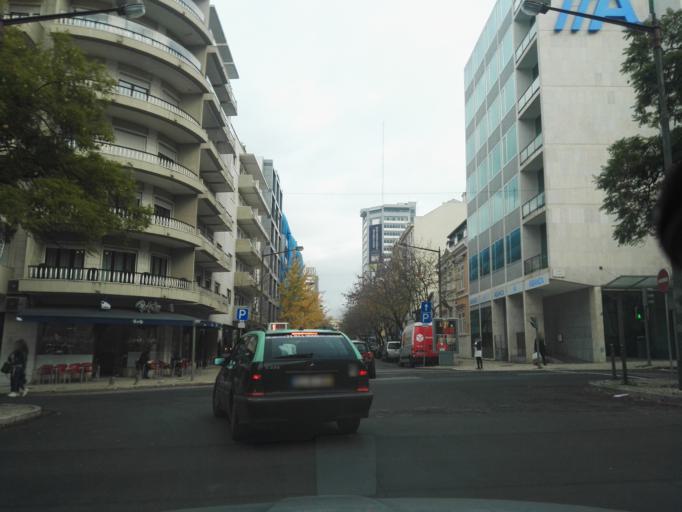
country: PT
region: Lisbon
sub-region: Lisbon
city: Lisbon
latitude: 38.7360
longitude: -9.1477
